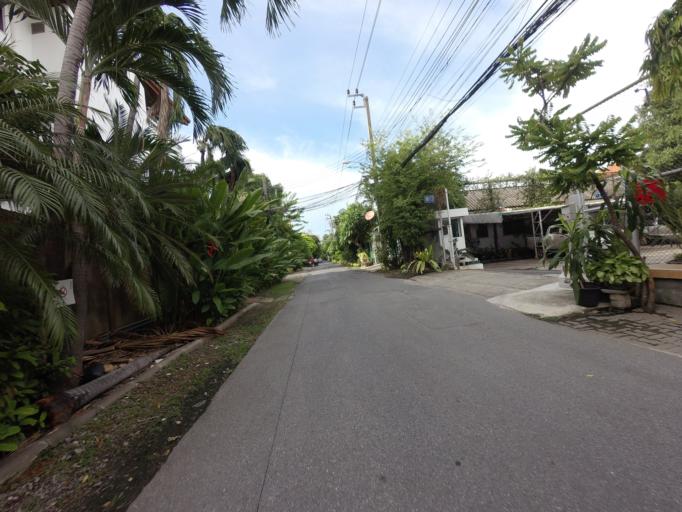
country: TH
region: Bangkok
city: Watthana
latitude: 13.7483
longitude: 100.5860
